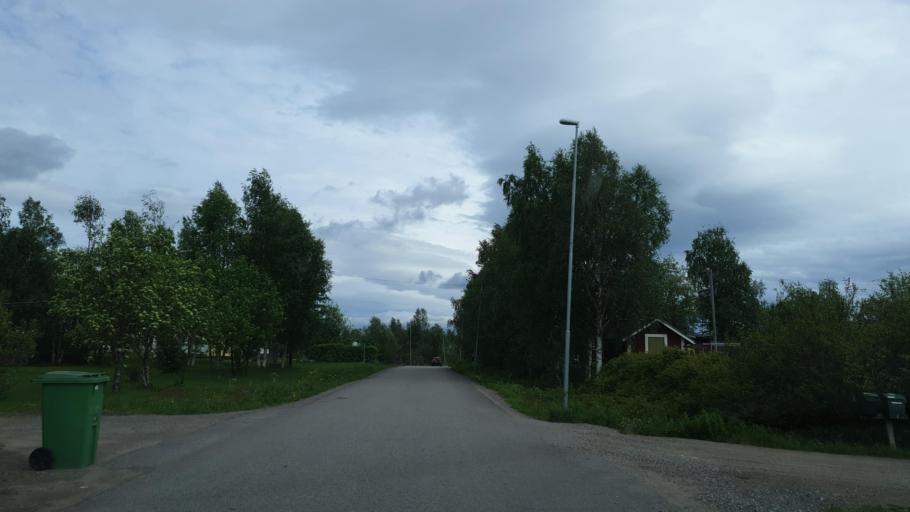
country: SE
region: Norrbotten
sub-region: Gallivare Kommun
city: Gaellivare
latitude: 67.1319
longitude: 20.6363
